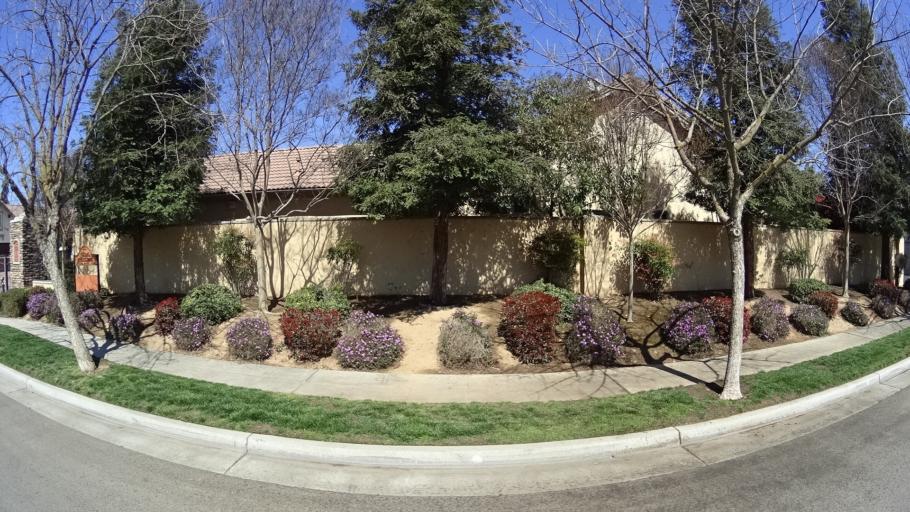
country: US
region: California
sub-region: Fresno County
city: Fresno
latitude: 36.8121
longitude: -119.8032
